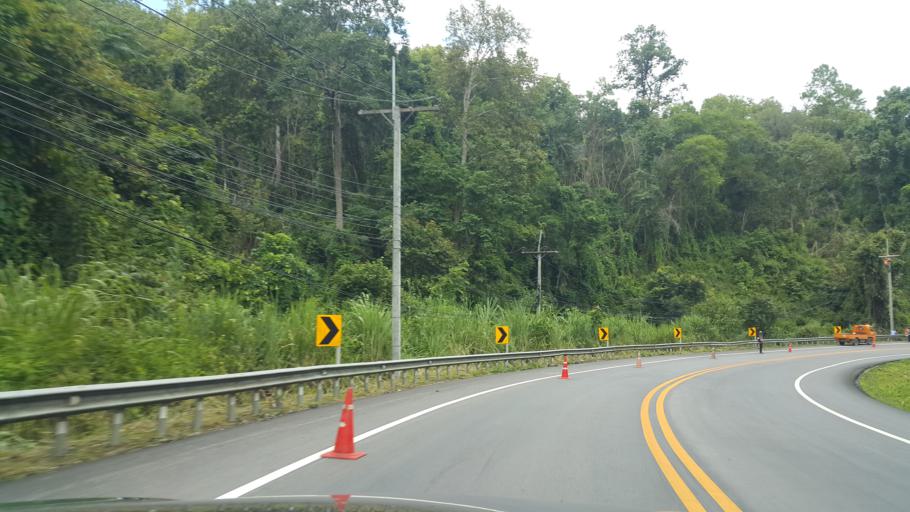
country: TH
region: Lampang
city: Wang Nuea
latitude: 19.0817
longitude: 99.3992
